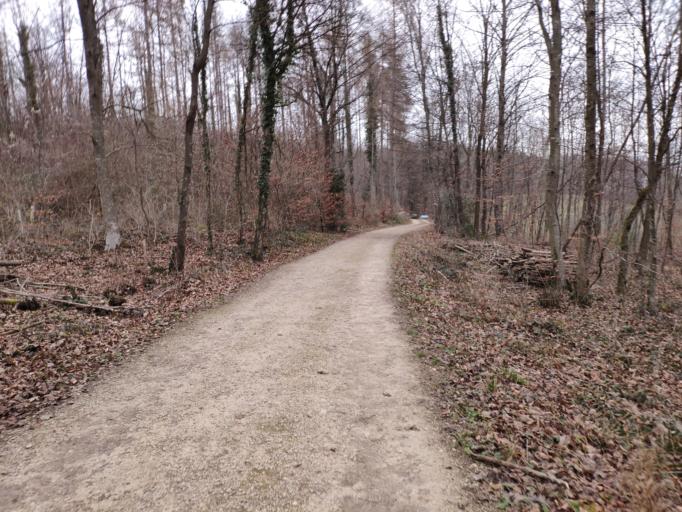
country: CH
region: Basel-City
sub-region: Basel-Stadt
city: Bettingen
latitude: 47.5786
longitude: 7.6777
